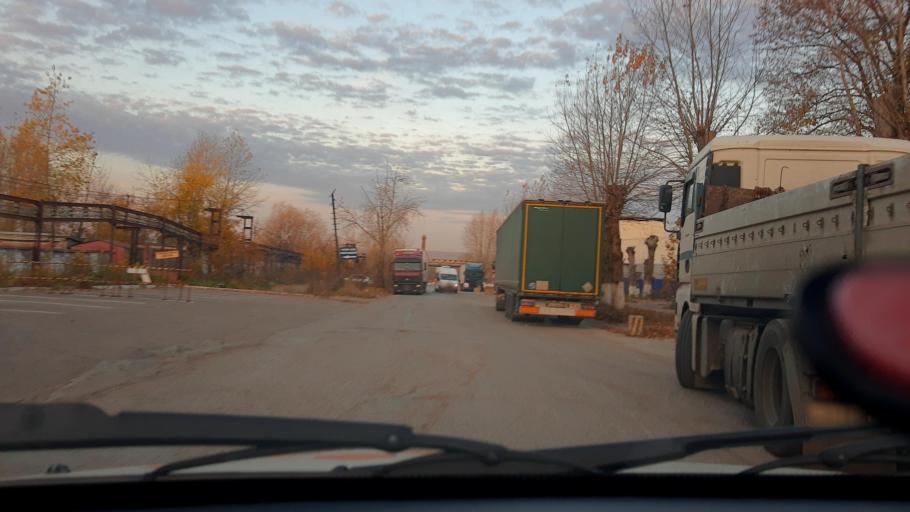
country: RU
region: Bashkortostan
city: Ufa
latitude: 54.8392
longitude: 56.0849
